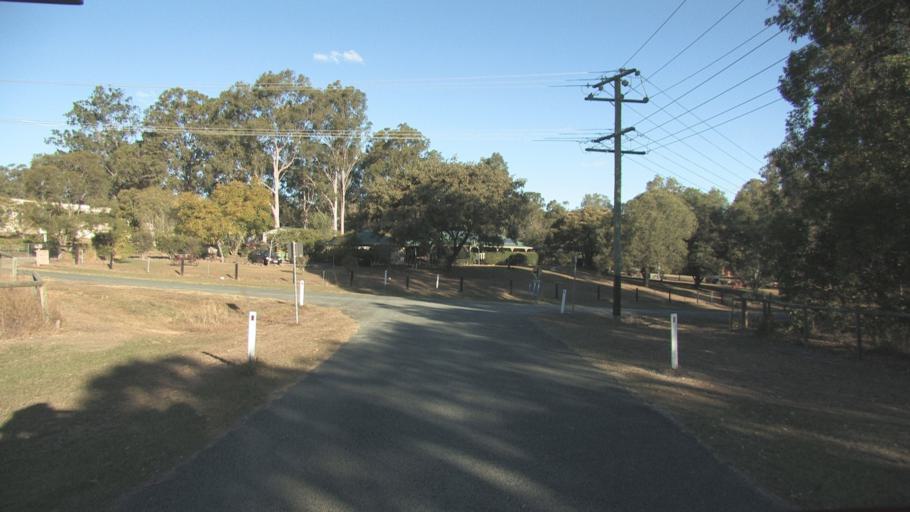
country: AU
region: Queensland
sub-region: Logan
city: Cedar Vale
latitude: -27.8568
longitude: 152.9810
